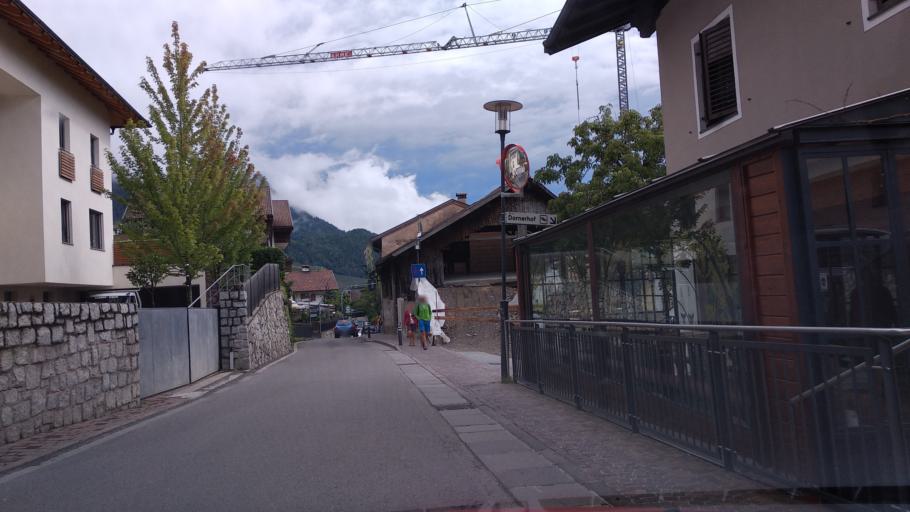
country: IT
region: Trentino-Alto Adige
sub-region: Bolzano
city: Scena
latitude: 46.6855
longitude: 11.1889
